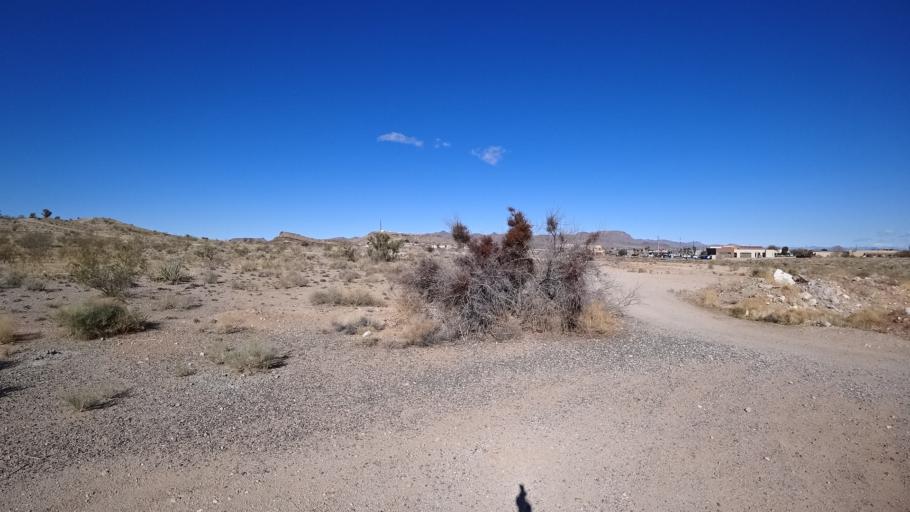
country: US
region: Arizona
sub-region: Mohave County
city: Kingman
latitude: 35.1897
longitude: -114.0260
